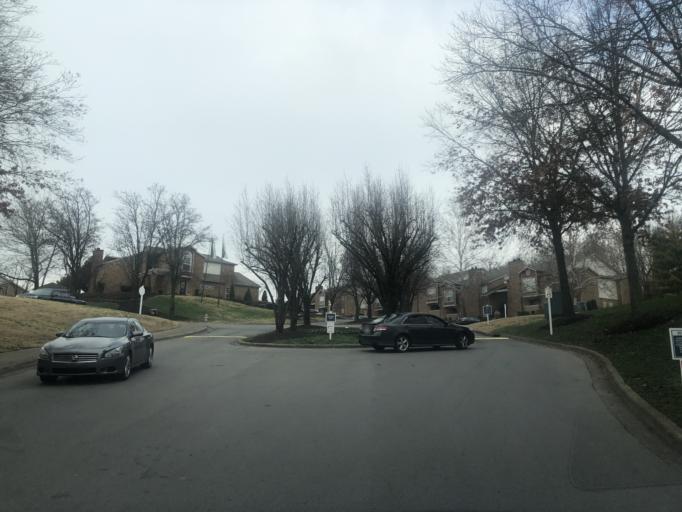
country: US
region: Tennessee
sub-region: Rutherford County
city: La Vergne
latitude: 36.0609
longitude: -86.6416
